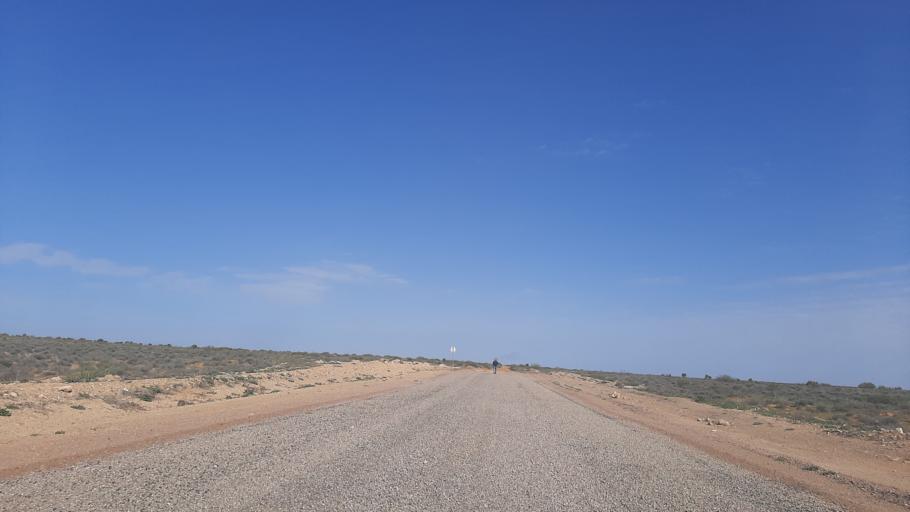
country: TN
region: Madanin
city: Medenine
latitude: 33.2426
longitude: 10.7402
